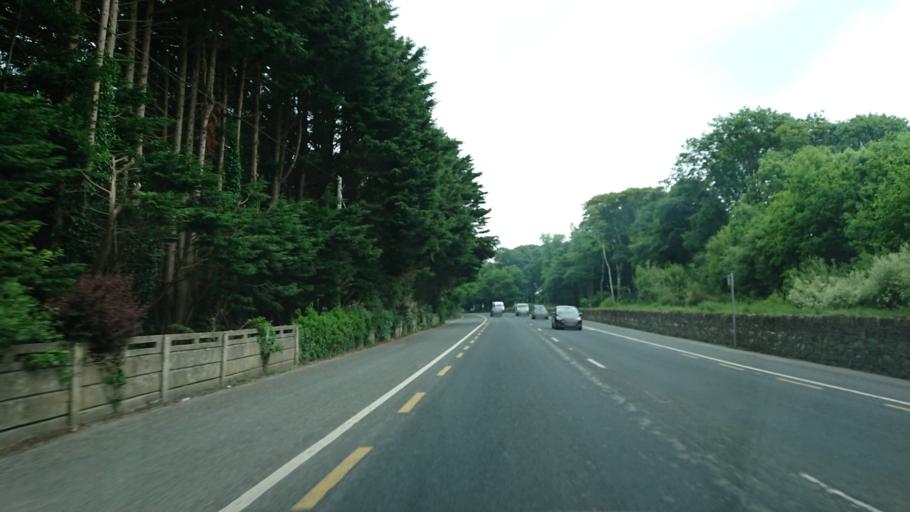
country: IE
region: Munster
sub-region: Waterford
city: Waterford
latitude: 52.2079
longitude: -7.1162
